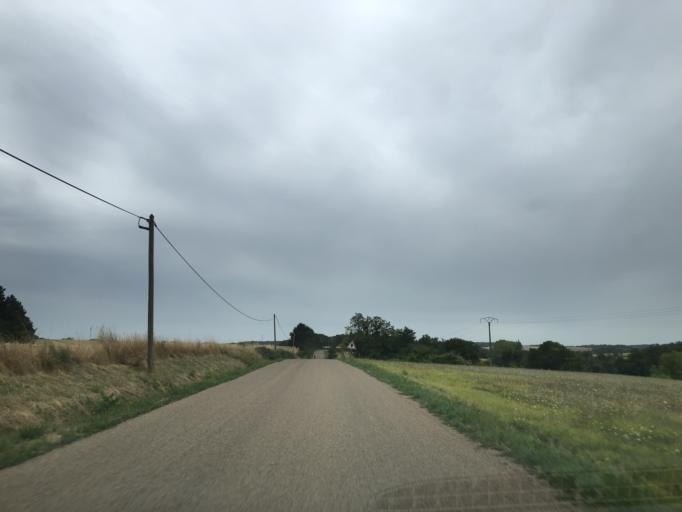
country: FR
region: Bourgogne
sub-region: Departement de l'Yonne
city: Charny
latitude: 47.9523
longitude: 3.1350
